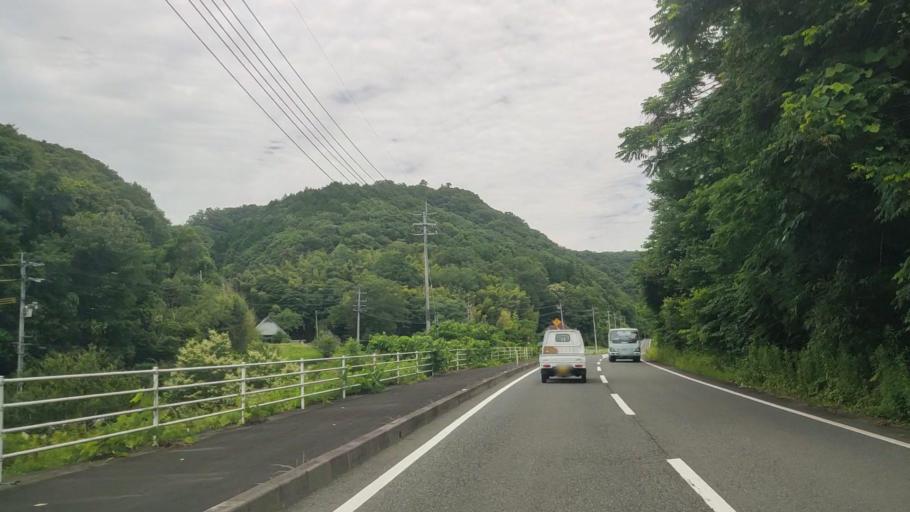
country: JP
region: Okayama
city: Tsuyama
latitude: 35.0652
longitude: 134.2204
